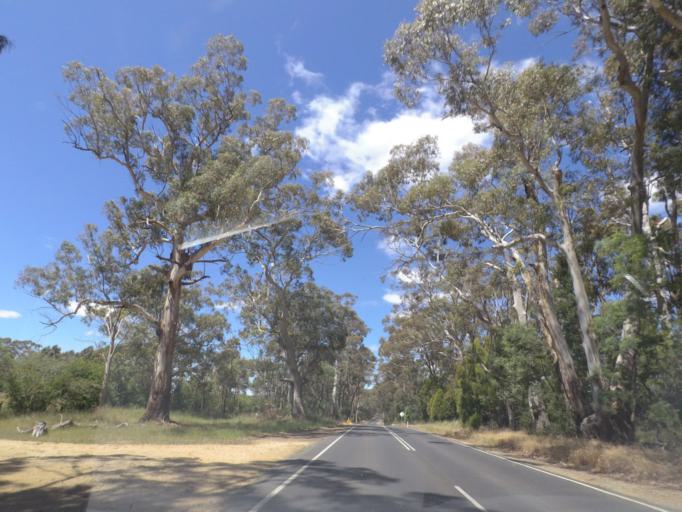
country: AU
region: Victoria
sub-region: Mount Alexander
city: Castlemaine
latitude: -37.2888
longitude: 144.2708
